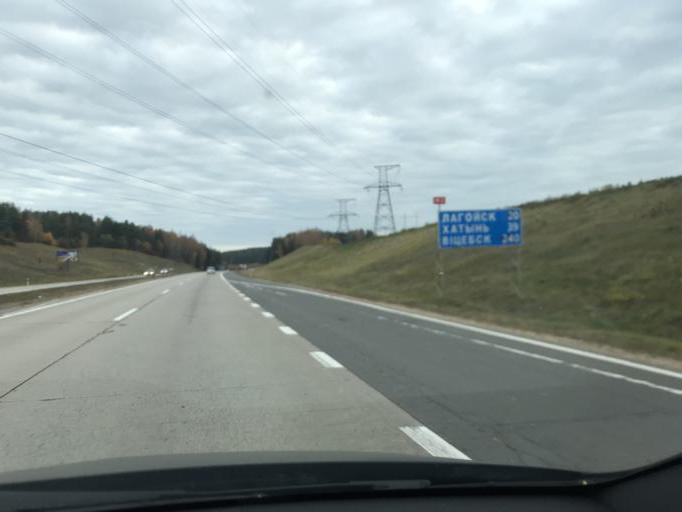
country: BY
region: Minsk
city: Astrashytski Haradok
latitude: 54.0587
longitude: 27.7073
